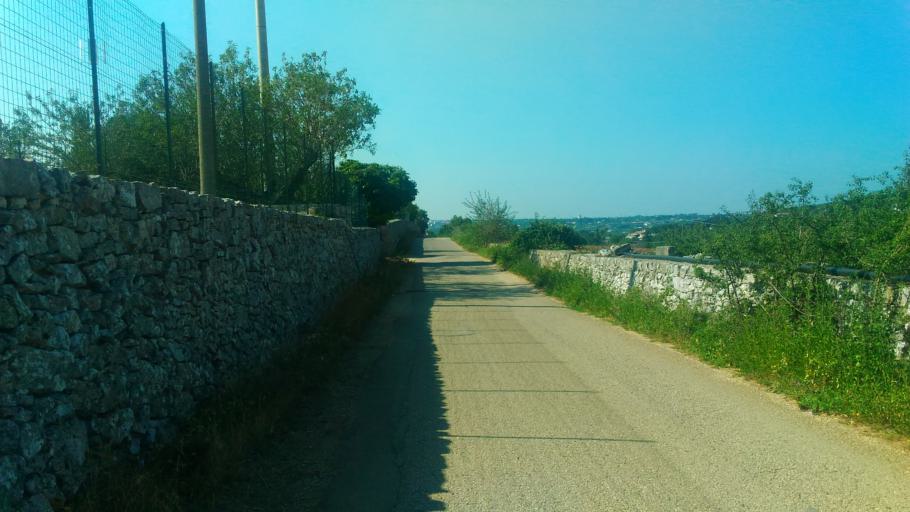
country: IT
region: Apulia
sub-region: Provincia di Bari
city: Noci
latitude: 40.8178
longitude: 17.1648
